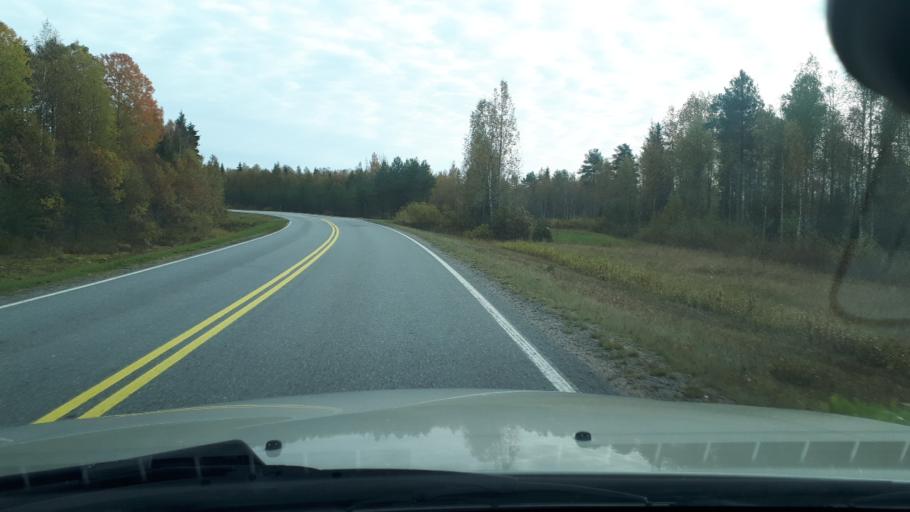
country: FI
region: Lapland
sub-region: Rovaniemi
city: Ranua
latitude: 66.0007
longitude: 26.2342
